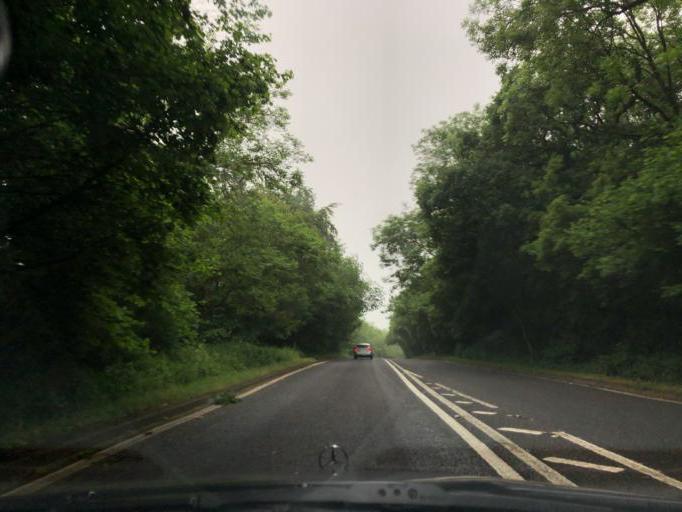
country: GB
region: England
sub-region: Warwickshire
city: Harbury
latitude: 52.2085
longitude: -1.4992
